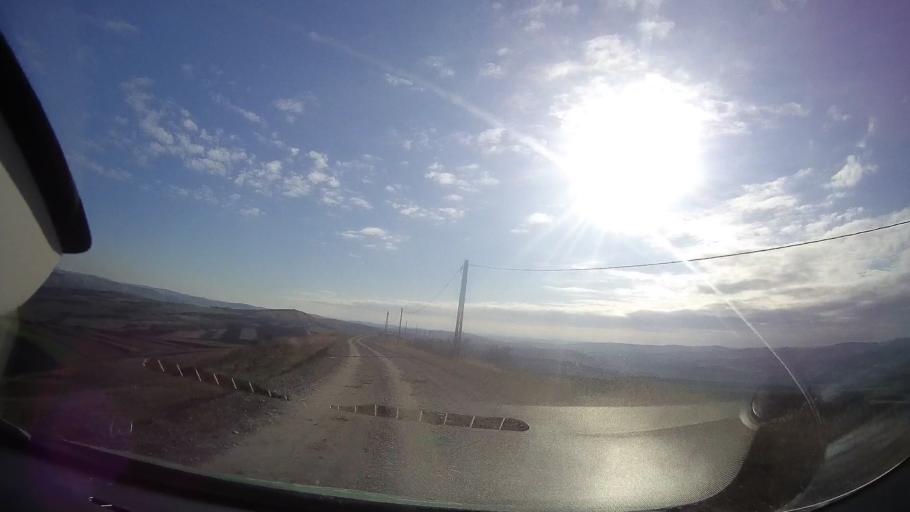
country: RO
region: Mures
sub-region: Comuna Saulia
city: Saulia
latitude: 46.5906
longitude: 24.2204
